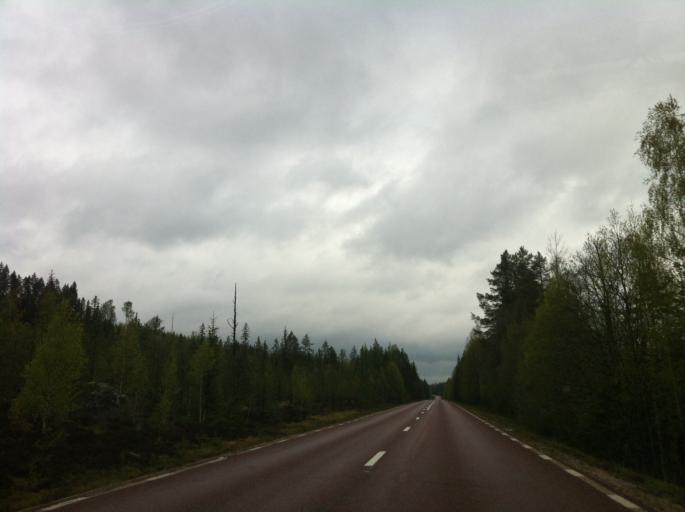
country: SE
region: Jaemtland
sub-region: Harjedalens Kommun
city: Sveg
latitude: 61.8766
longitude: 14.6288
